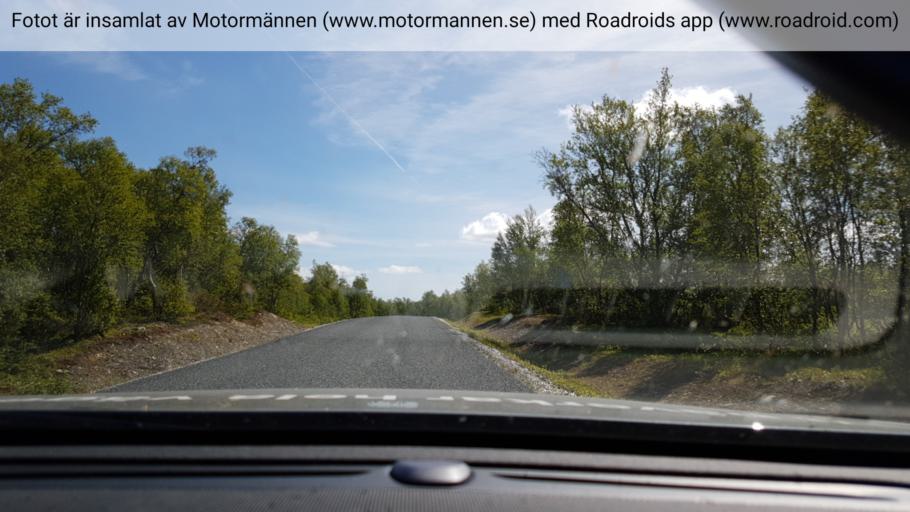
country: NO
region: Nordland
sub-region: Hattfjelldal
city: Hattfjelldal
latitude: 65.4021
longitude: 14.9567
